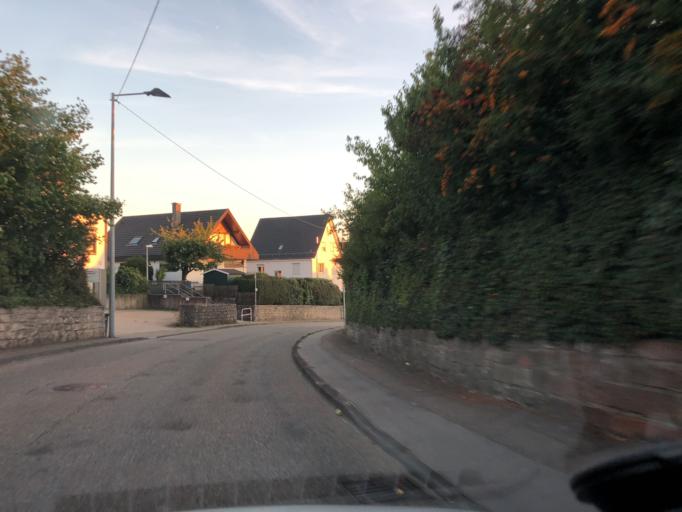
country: DE
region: Baden-Wuerttemberg
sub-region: Regierungsbezirk Stuttgart
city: Marbach am Neckar
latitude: 48.9072
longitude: 9.2658
